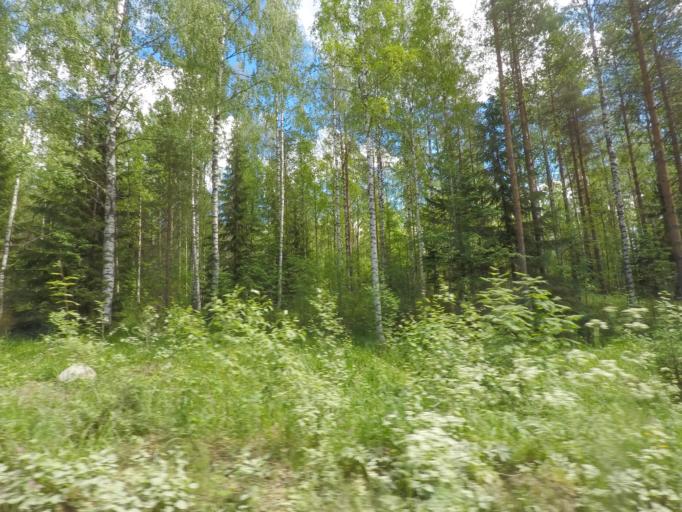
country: FI
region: Central Finland
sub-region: Jyvaeskylae
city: Hankasalmi
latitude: 62.4326
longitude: 26.6484
